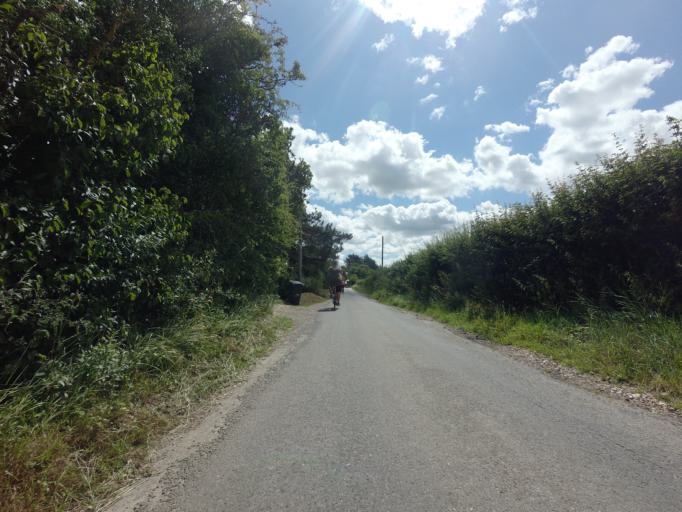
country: GB
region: England
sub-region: East Sussex
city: Ringmer
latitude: 50.8630
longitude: 0.1430
